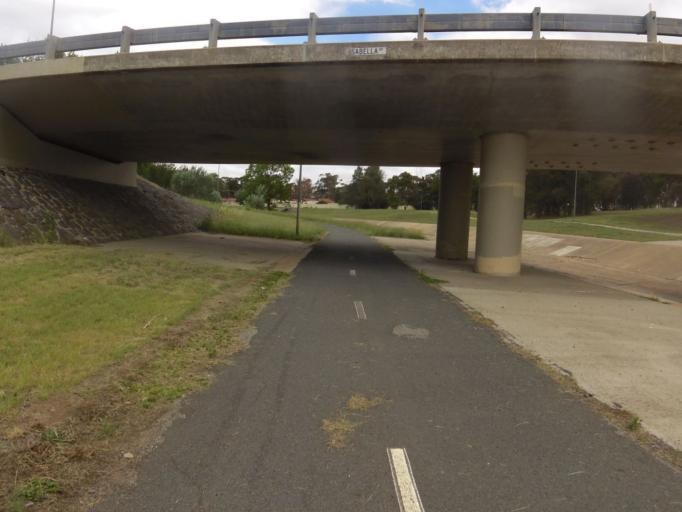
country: AU
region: Australian Capital Territory
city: Macarthur
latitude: -35.4217
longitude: 149.0945
